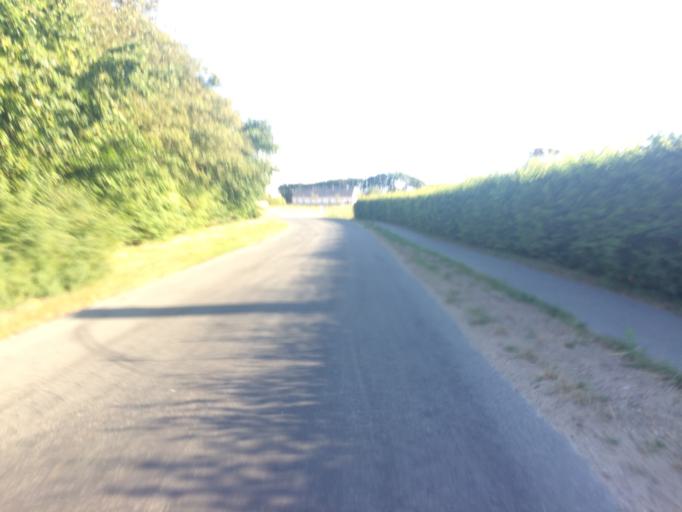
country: DK
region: Central Jutland
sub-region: Holstebro Kommune
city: Vinderup
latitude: 56.6018
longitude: 8.7716
